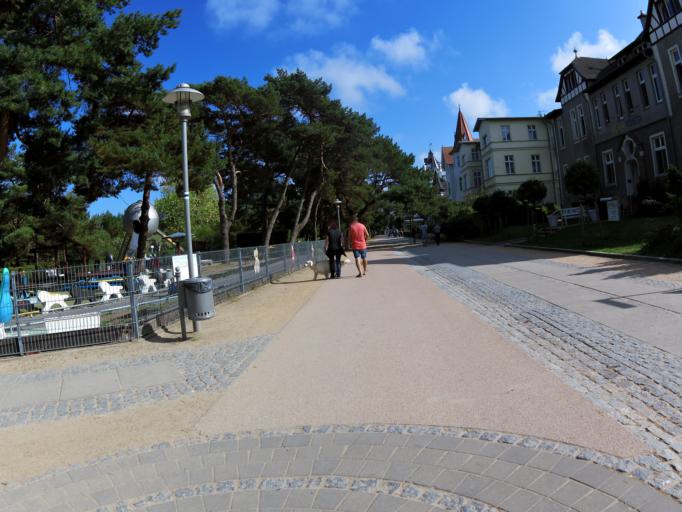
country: DE
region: Mecklenburg-Vorpommern
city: Ostseebad Zinnowitz
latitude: 54.0824
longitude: 13.9112
